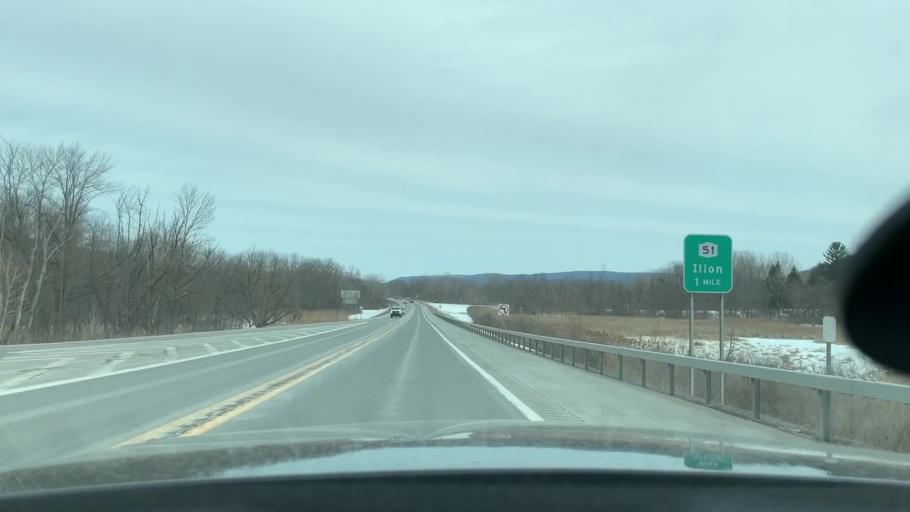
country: US
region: New York
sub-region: Herkimer County
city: Ilion
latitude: 43.0227
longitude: -75.0502
